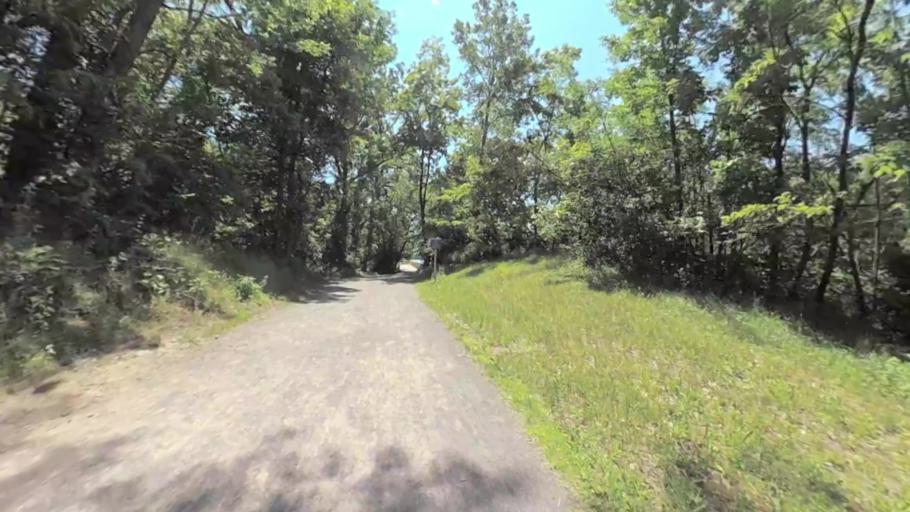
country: US
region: New York
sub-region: Monroe County
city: Pittsford
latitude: 43.0800
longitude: -77.5018
